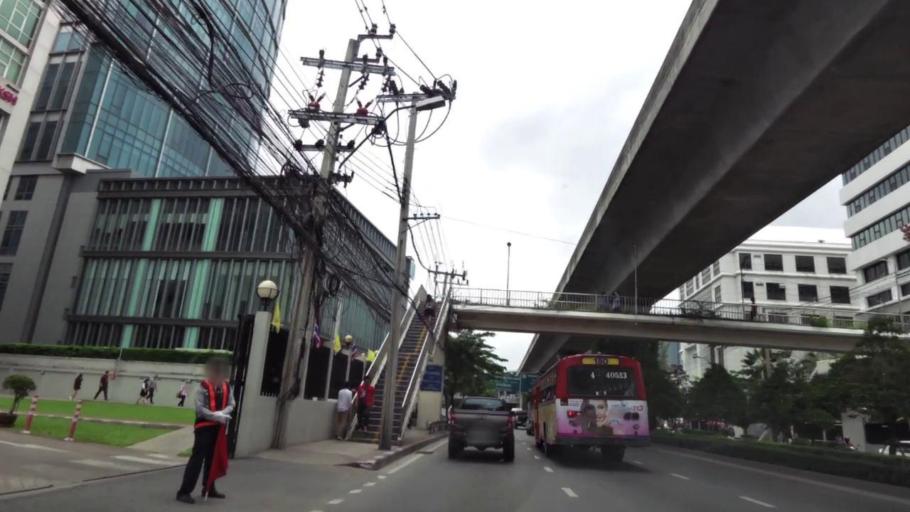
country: TH
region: Bangkok
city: Phra Khanong
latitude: 13.6940
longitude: 100.6065
